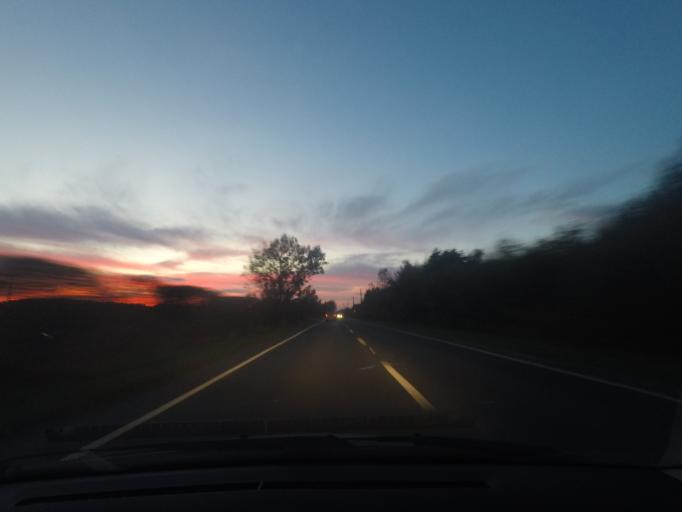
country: GB
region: England
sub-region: East Riding of Yorkshire
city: Thornton
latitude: 53.9353
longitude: -0.8488
